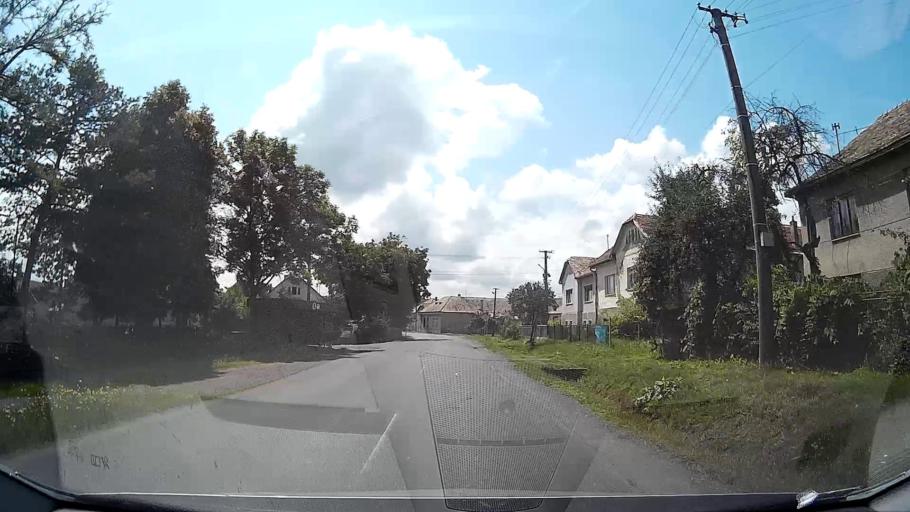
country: SK
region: Banskobystricky
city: Fil'akovo
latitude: 48.3004
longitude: 19.7912
